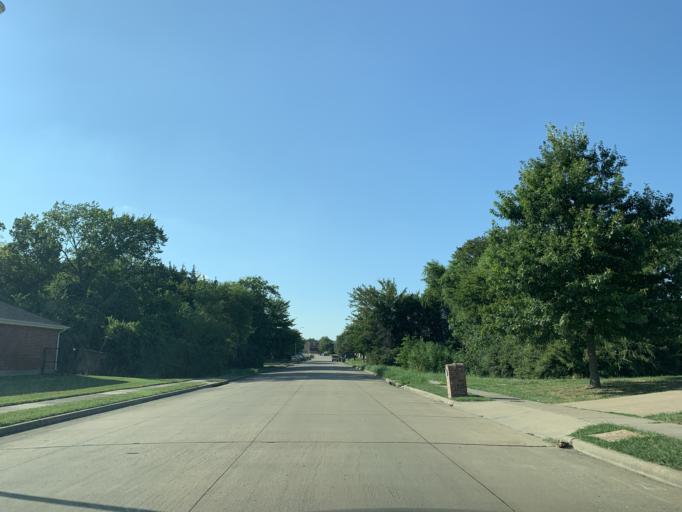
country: US
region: Texas
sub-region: Dallas County
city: Hutchins
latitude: 32.6550
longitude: -96.7650
